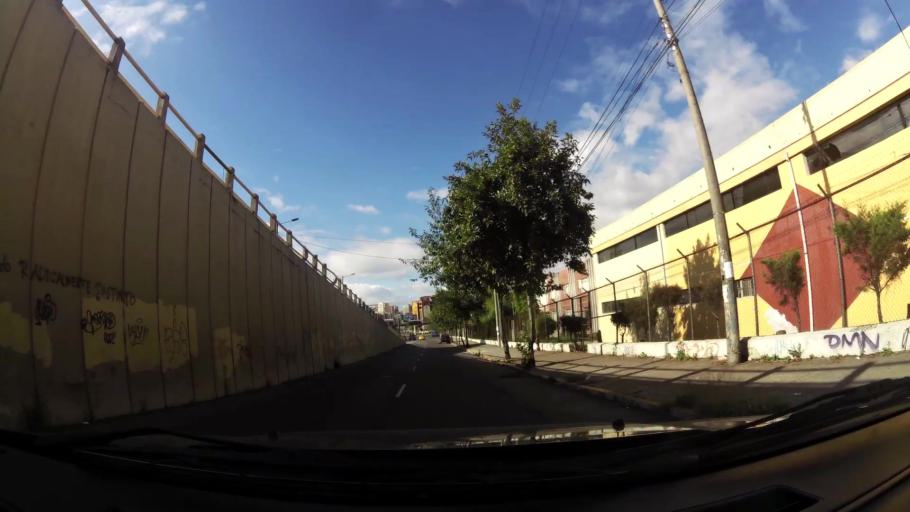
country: EC
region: Pichincha
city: Quito
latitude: -0.2150
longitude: -78.4903
